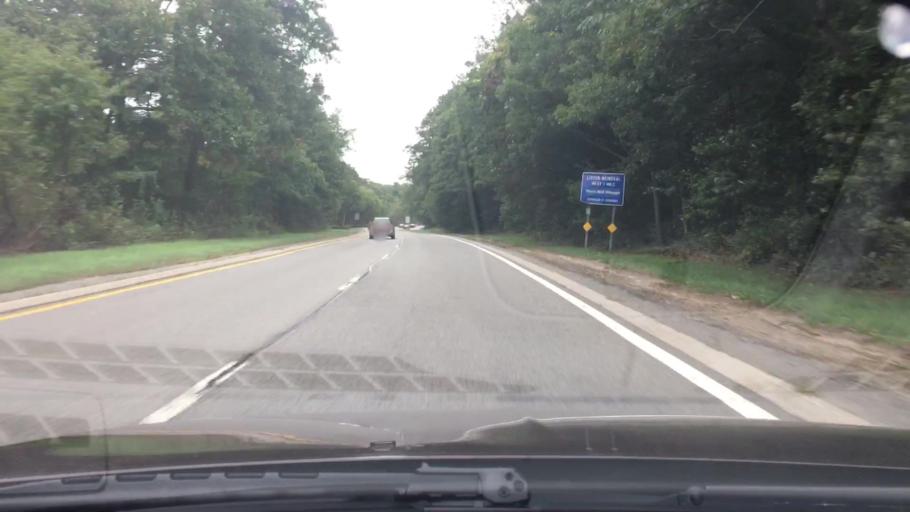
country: US
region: New York
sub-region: Suffolk County
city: South Huntington
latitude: 40.8188
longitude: -73.3717
